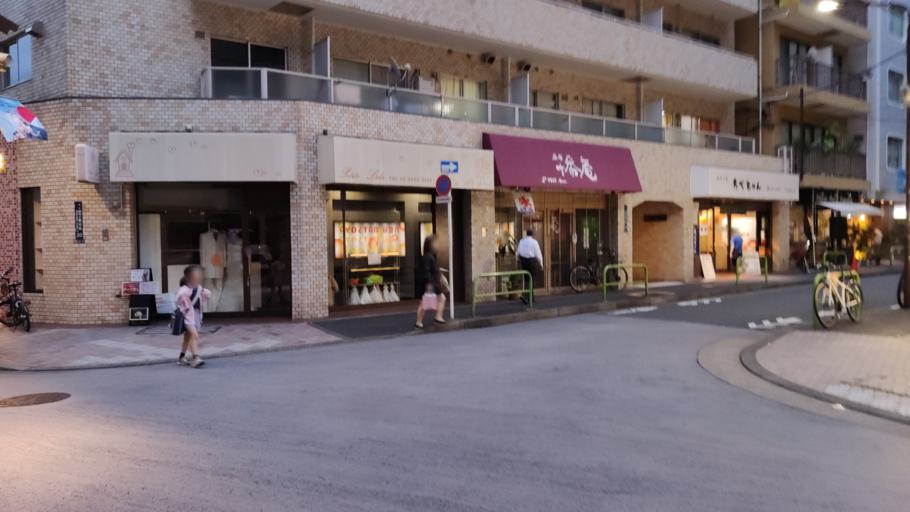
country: JP
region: Tokyo
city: Tokyo
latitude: 35.6551
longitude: 139.7363
